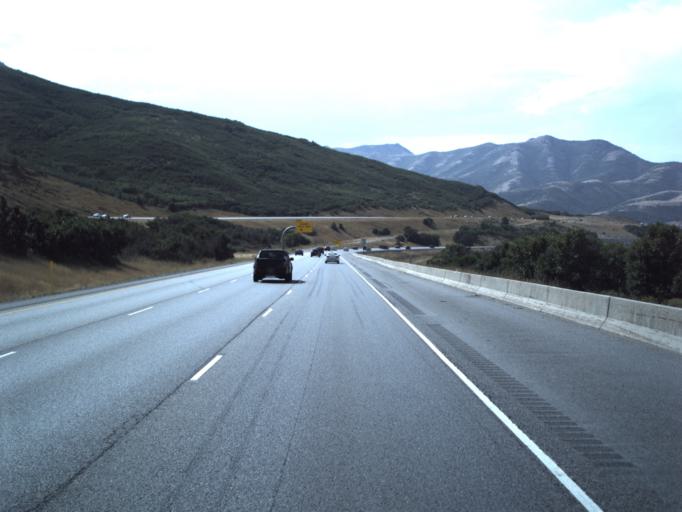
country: US
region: Utah
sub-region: Summit County
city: Summit Park
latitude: 40.7436
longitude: -111.6826
